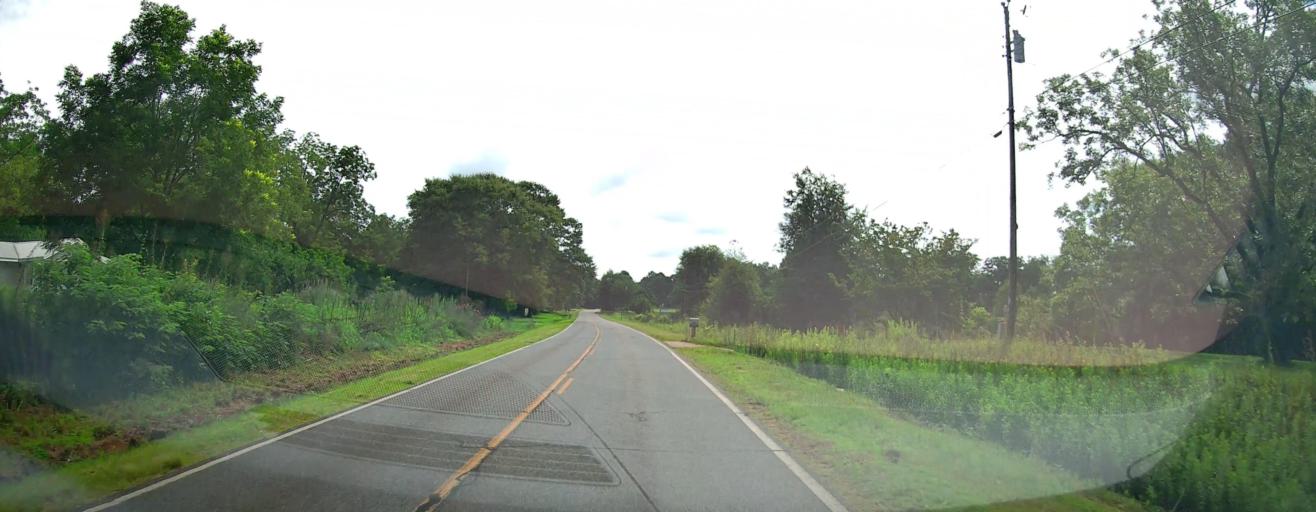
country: US
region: Georgia
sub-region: Peach County
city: Byron
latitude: 32.6430
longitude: -83.7905
